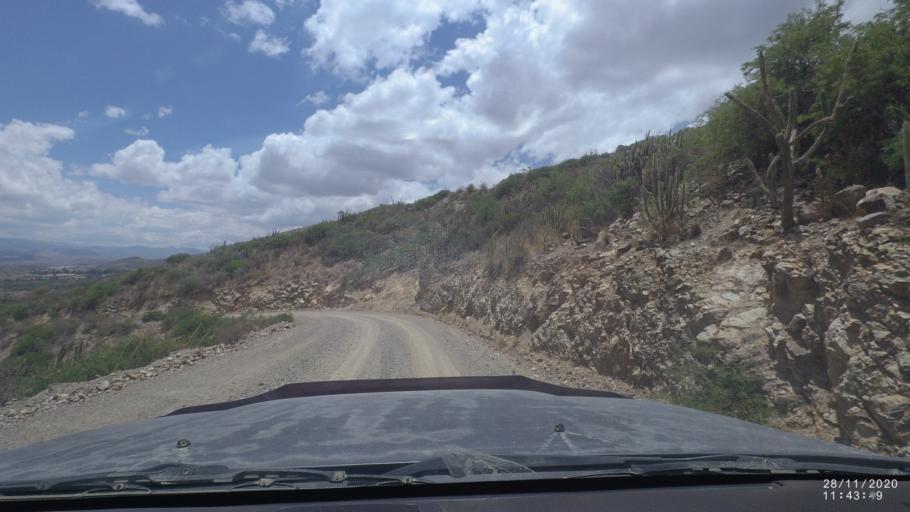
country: BO
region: Cochabamba
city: Tarata
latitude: -17.6608
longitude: -66.0455
